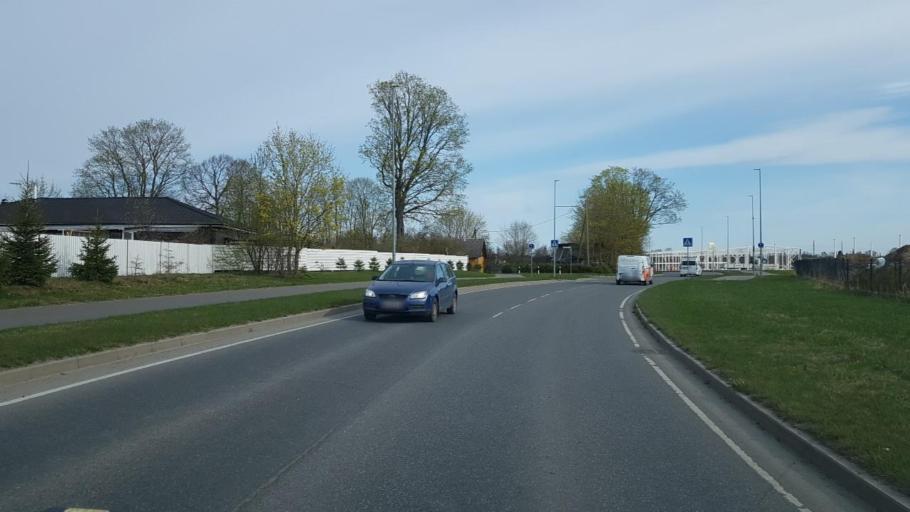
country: EE
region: Tartu
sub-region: UElenurme vald
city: Ulenurme
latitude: 58.3404
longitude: 26.7010
